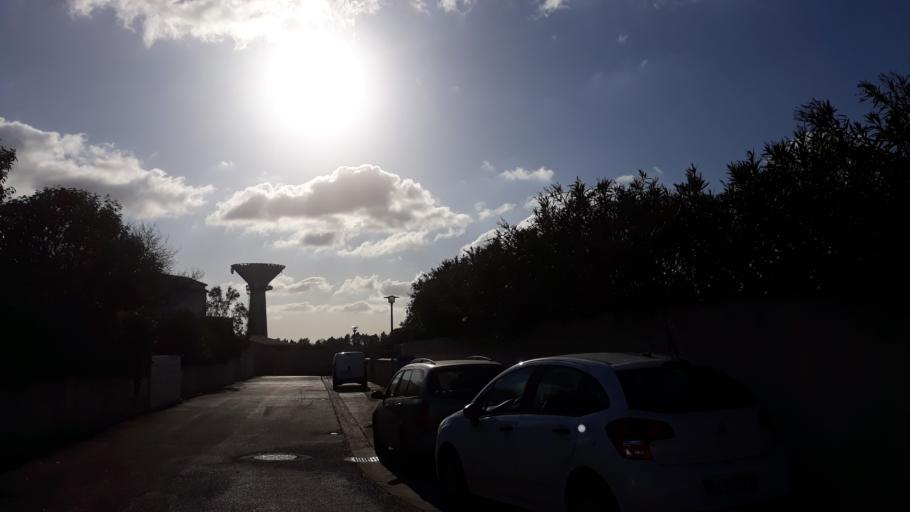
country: FR
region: Languedoc-Roussillon
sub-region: Departement du Gard
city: Aimargues
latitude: 43.6895
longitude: 4.2043
